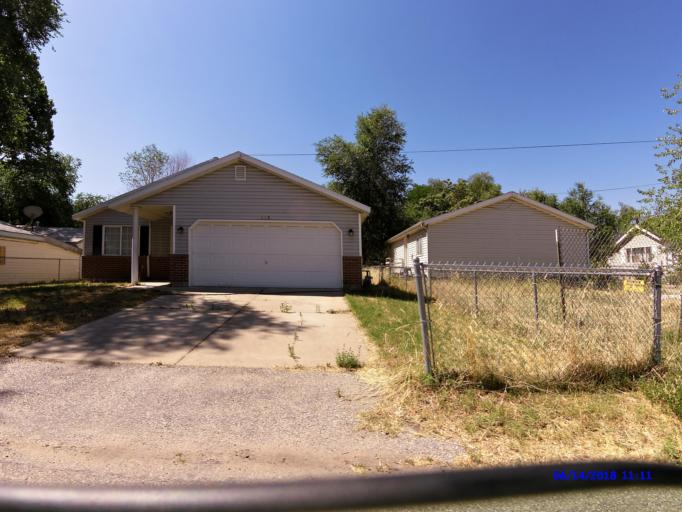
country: US
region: Utah
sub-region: Weber County
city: Ogden
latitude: 41.2194
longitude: -112.0000
